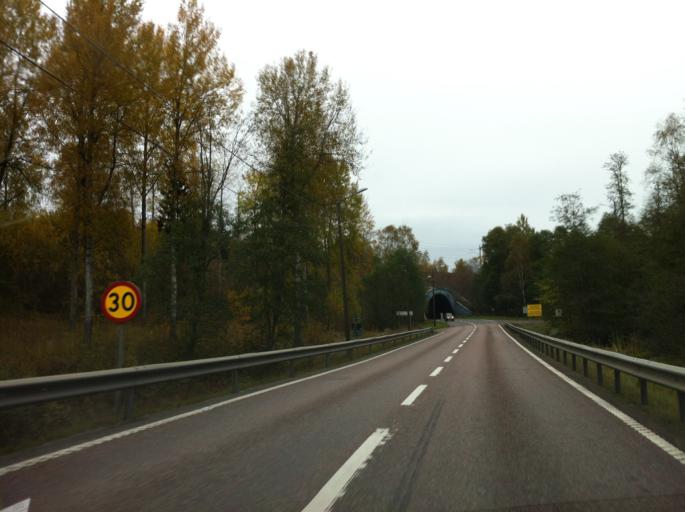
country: SE
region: Dalarna
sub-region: Ludvika Kommun
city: Grangesberg
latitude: 60.0598
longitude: 14.9863
